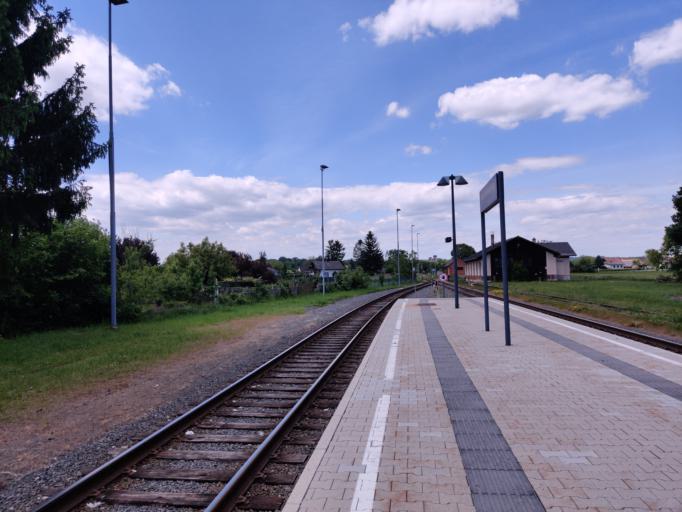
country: AT
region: Styria
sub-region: Politischer Bezirk Suedoststeiermark
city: Bad Radkersburg
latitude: 46.6998
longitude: 15.9931
